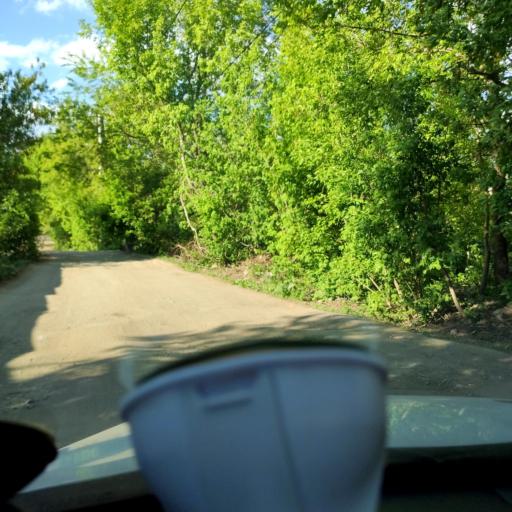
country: RU
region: Samara
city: Petra-Dubrava
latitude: 53.2565
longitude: 50.3438
